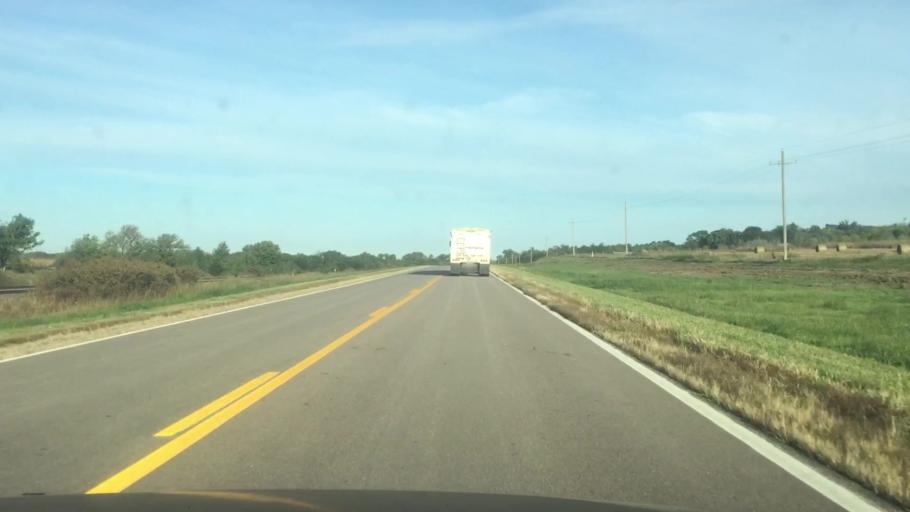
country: US
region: Nebraska
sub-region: Jefferson County
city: Fairbury
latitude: 40.0562
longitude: -97.0403
